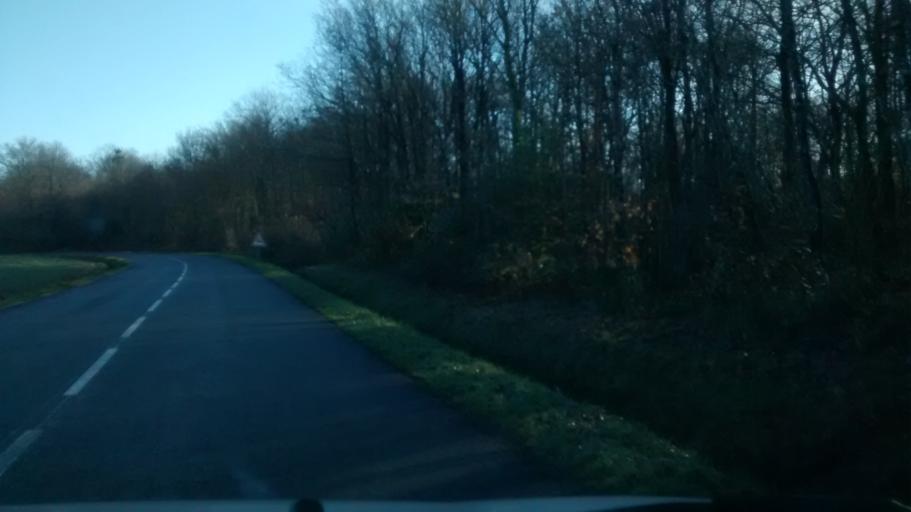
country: FR
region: Centre
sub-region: Departement d'Indre-et-Loire
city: Monnaie
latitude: 47.4955
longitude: 0.8063
